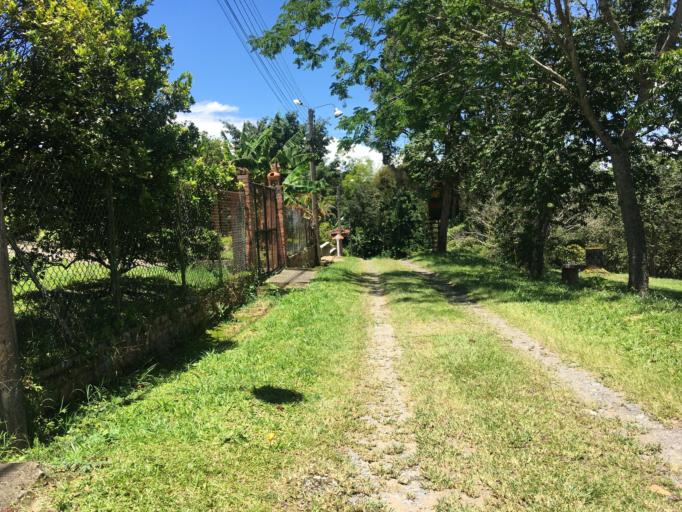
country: CO
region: Santander
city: Barbosa
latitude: 5.9184
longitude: -73.6040
